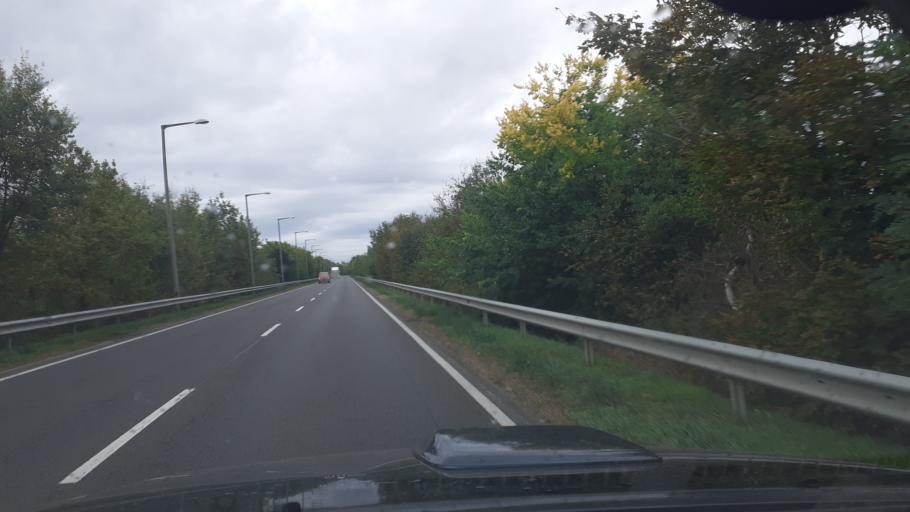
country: HU
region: Tolna
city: Dunafoldvar
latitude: 46.8000
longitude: 18.9273
